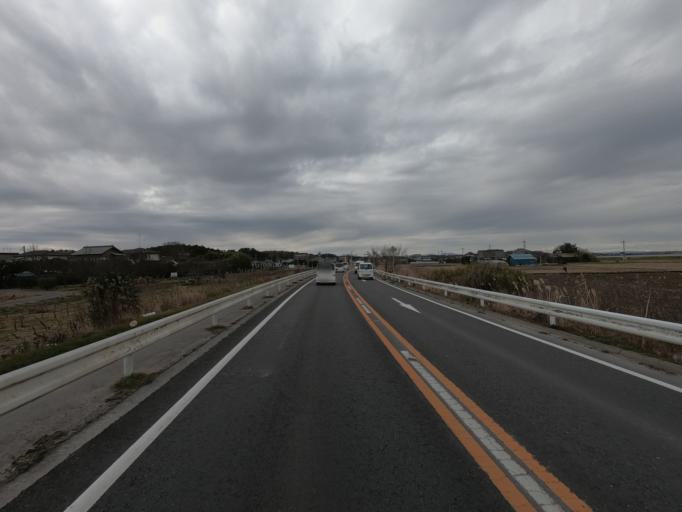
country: JP
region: Ibaraki
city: Inashiki
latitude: 36.0881
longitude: 140.3871
